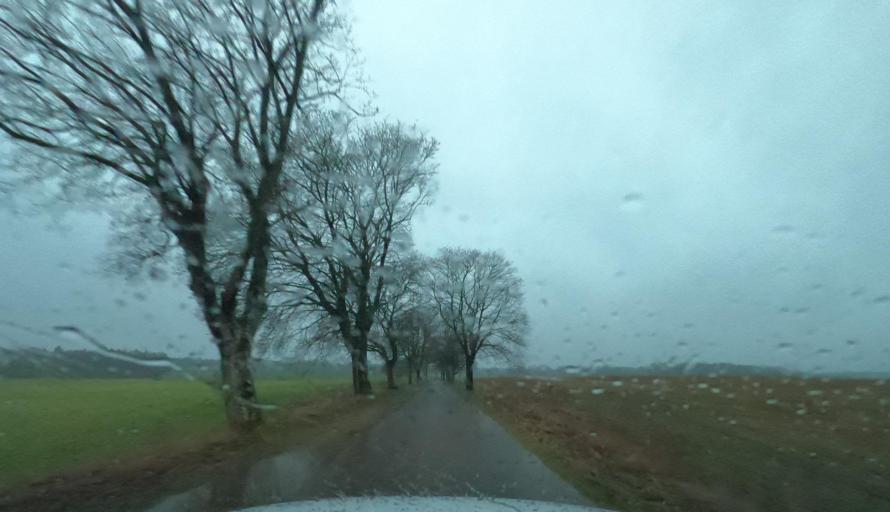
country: PL
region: West Pomeranian Voivodeship
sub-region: Powiat szczecinecki
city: Borne Sulinowo
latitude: 53.7008
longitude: 16.5123
